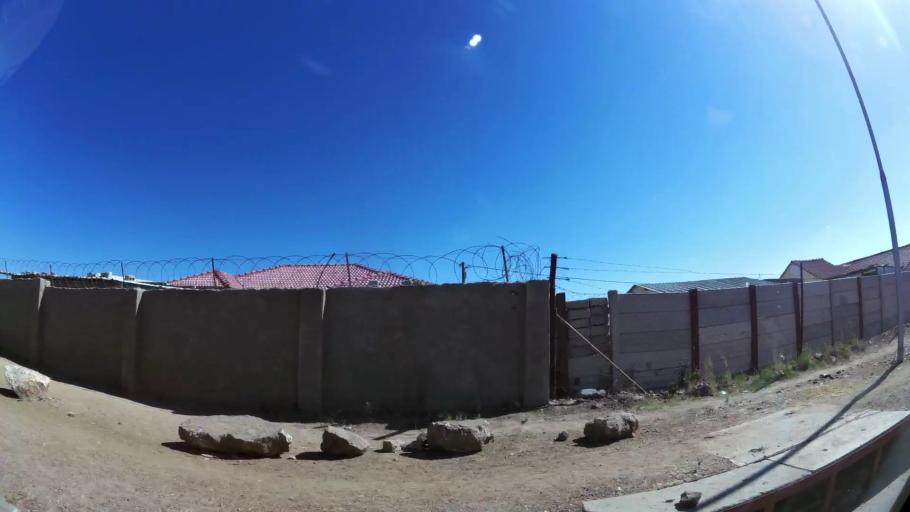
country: ZA
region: Limpopo
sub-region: Capricorn District Municipality
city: Polokwane
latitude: -23.8553
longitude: 29.4133
